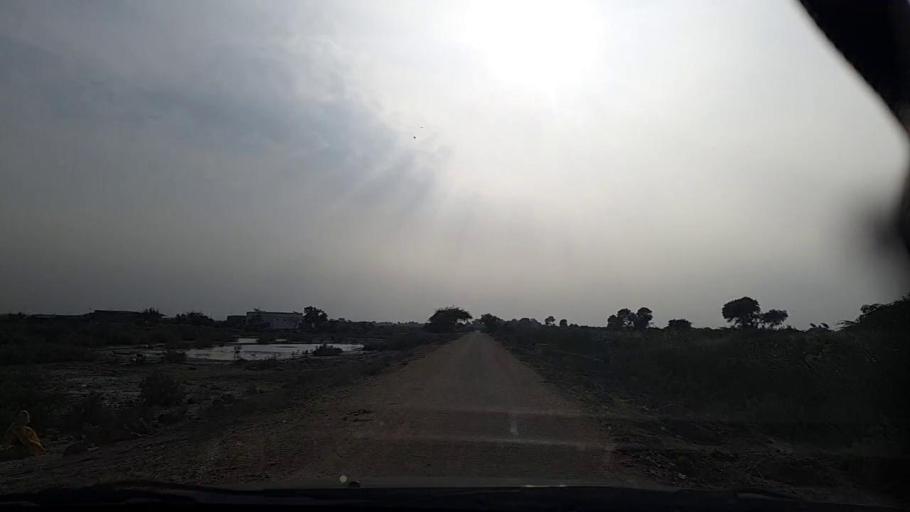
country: PK
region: Sindh
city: Thatta
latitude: 24.7099
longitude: 67.9321
